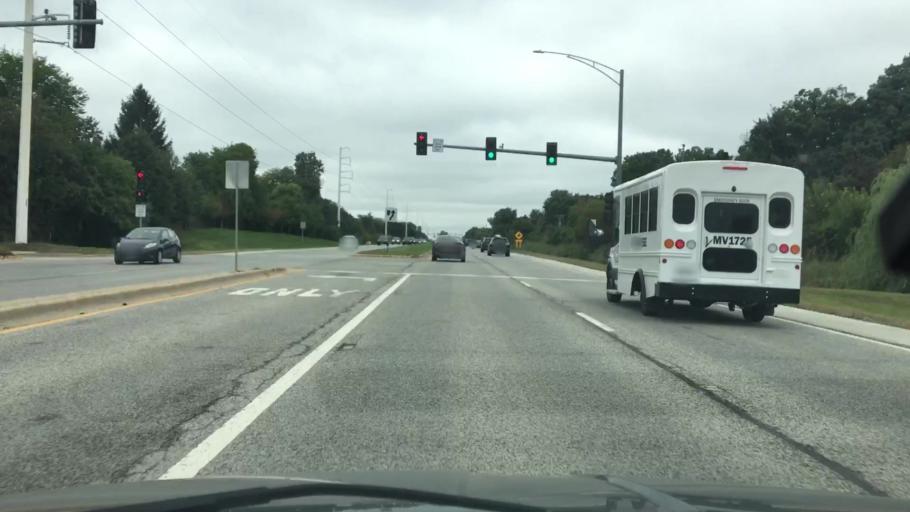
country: US
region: Illinois
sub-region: DuPage County
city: Woodridge
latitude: 41.7492
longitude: -88.0944
